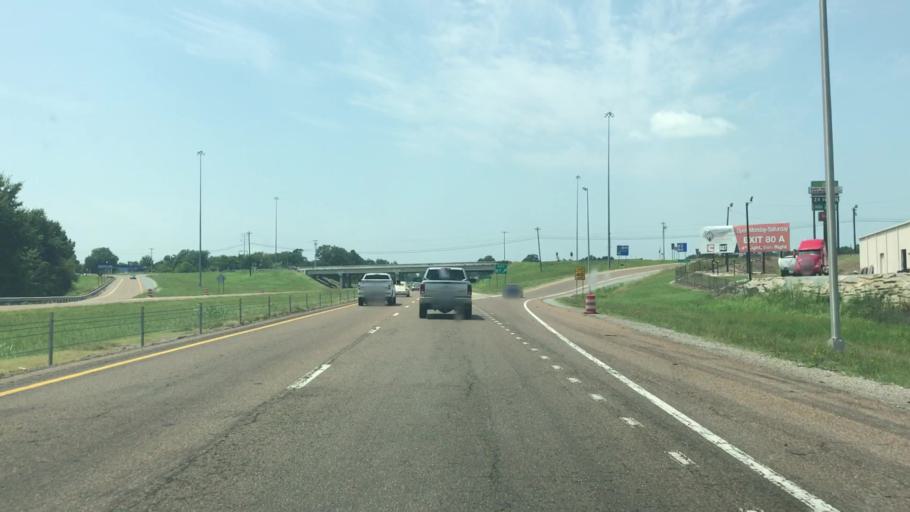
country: US
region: Tennessee
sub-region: Madison County
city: Jackson
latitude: 35.6812
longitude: -88.7395
